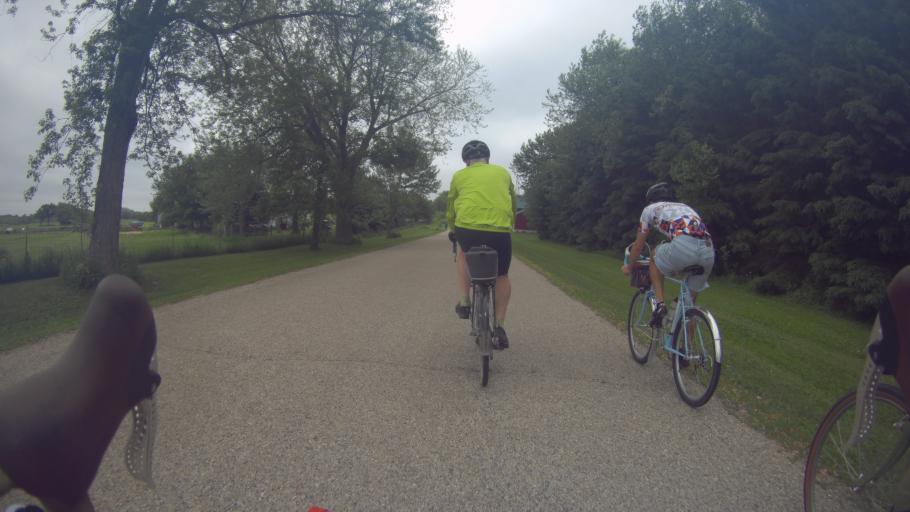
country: US
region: Wisconsin
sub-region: Green County
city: Brooklyn
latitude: 42.8849
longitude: -89.3783
